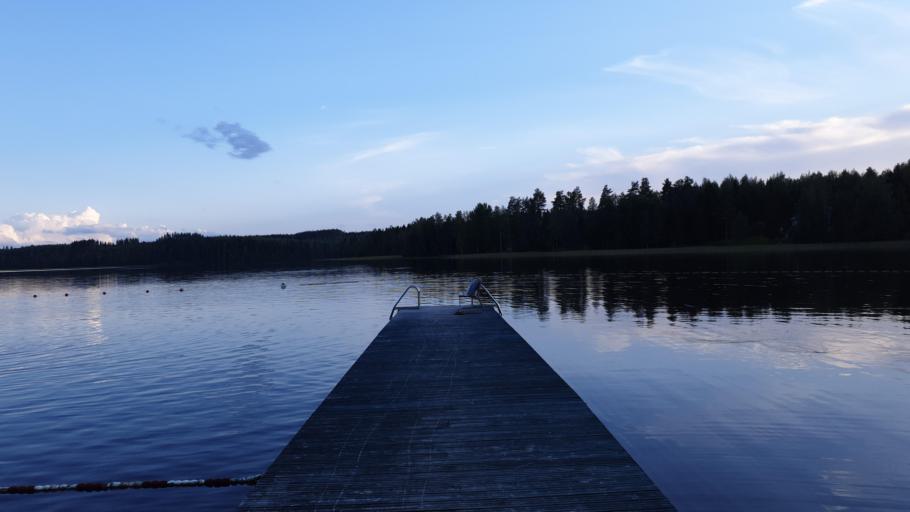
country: FI
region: Northern Savo
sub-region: Koillis-Savo
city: Kaavi
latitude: 62.9737
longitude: 28.4679
